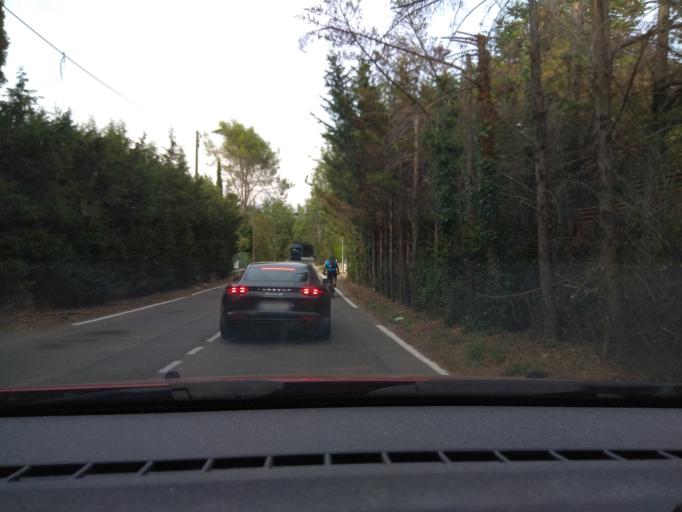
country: FR
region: Provence-Alpes-Cote d'Azur
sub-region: Departement des Alpes-Maritimes
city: Valbonne
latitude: 43.6463
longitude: 7.0218
